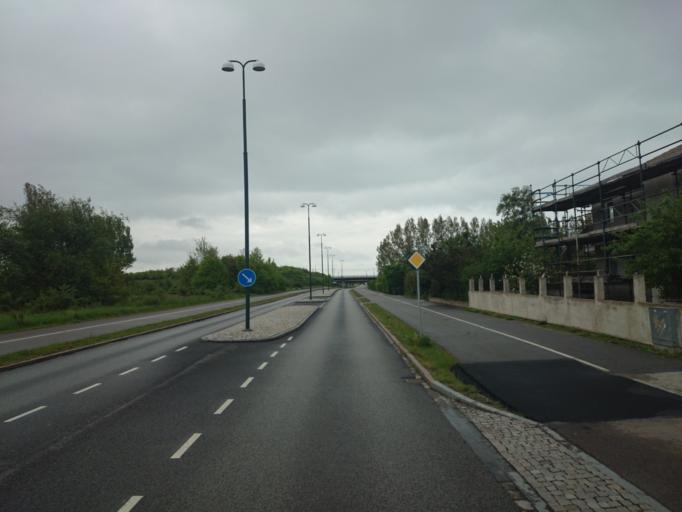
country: SE
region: Skane
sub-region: Malmo
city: Bunkeflostrand
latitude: 55.5683
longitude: 12.9219
